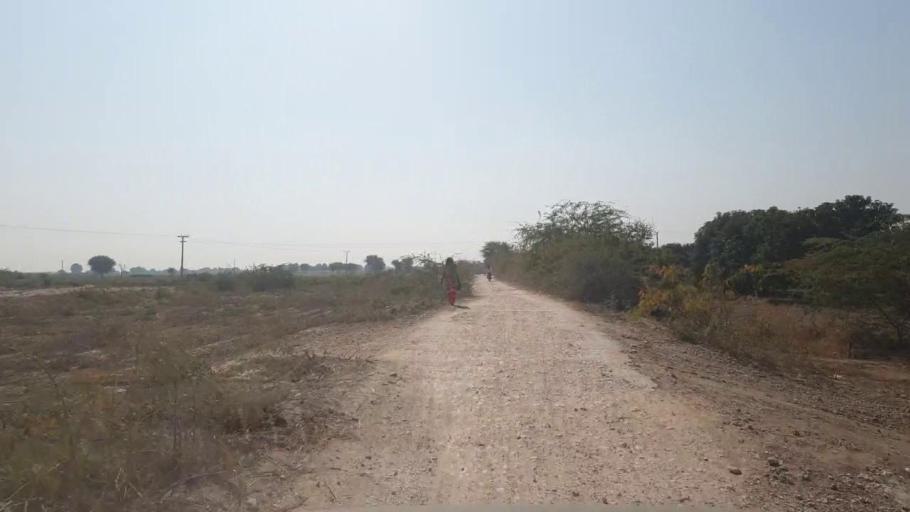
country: PK
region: Sindh
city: Chambar
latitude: 25.2428
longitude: 68.8276
